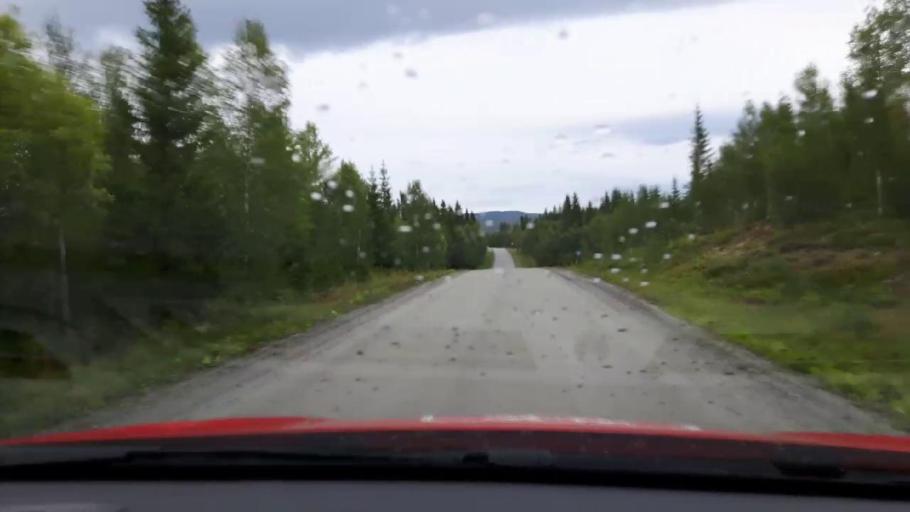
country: SE
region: Jaemtland
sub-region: Are Kommun
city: Are
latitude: 63.4440
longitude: 13.2217
